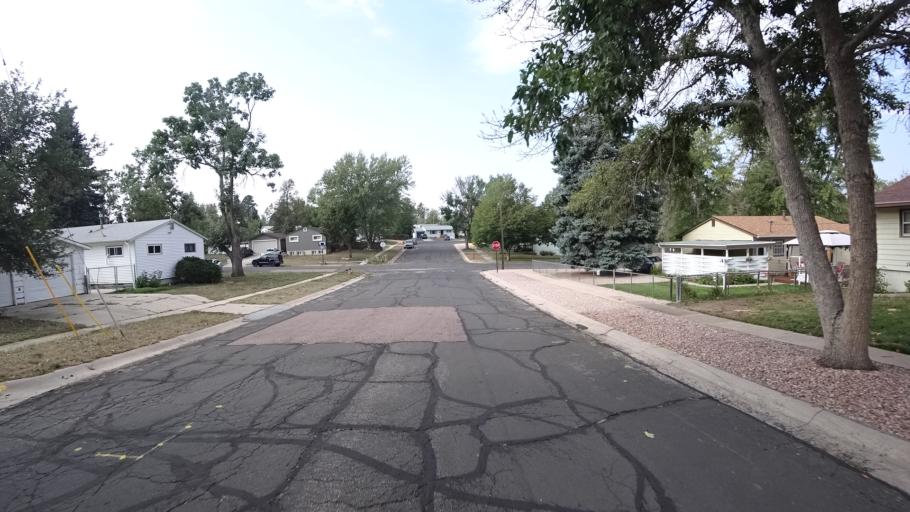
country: US
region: Colorado
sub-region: El Paso County
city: Colorado Springs
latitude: 38.8522
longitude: -104.7782
